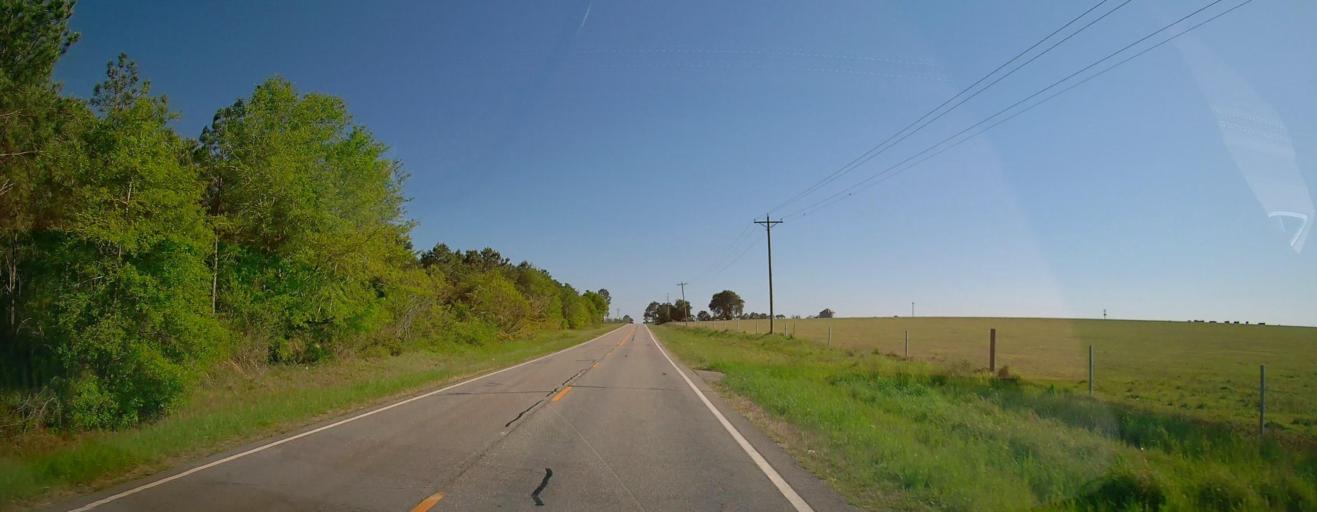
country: US
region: Georgia
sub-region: Wilcox County
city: Rochelle
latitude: 31.8634
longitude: -83.4888
